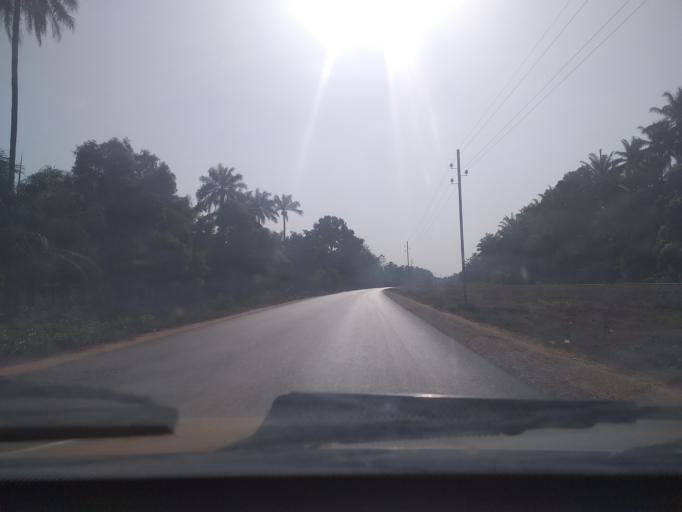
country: GN
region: Boke
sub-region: Boke Prefecture
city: Sangueya
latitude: 10.7785
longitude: -14.4445
